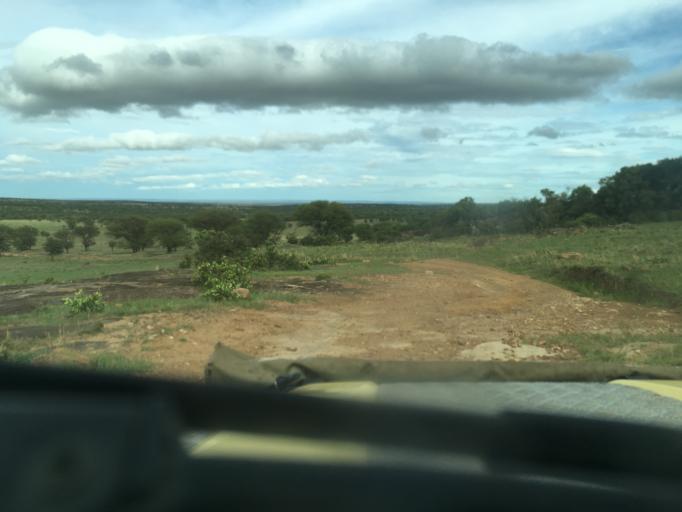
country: TZ
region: Mara
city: Mugumu
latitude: -1.9982
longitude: 35.1614
